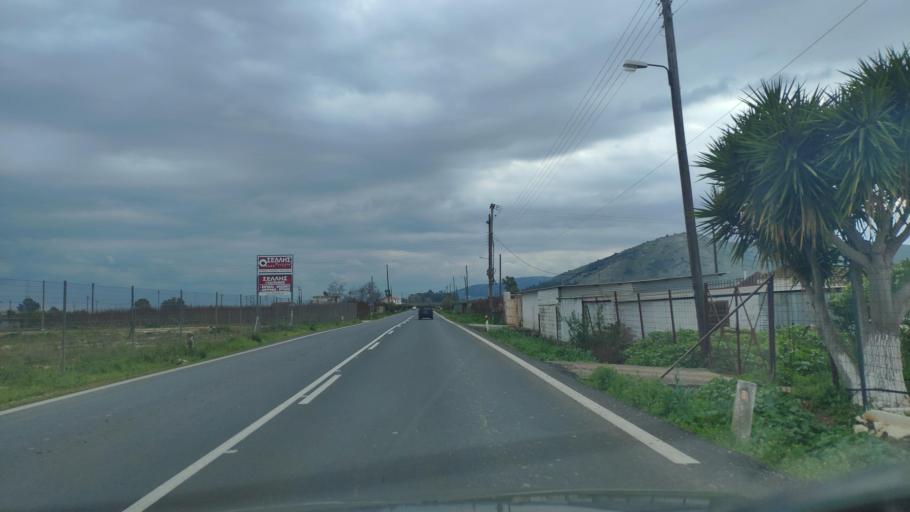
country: GR
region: Peloponnese
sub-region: Nomos Argolidos
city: Nea Kios
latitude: 37.5714
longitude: 22.7087
